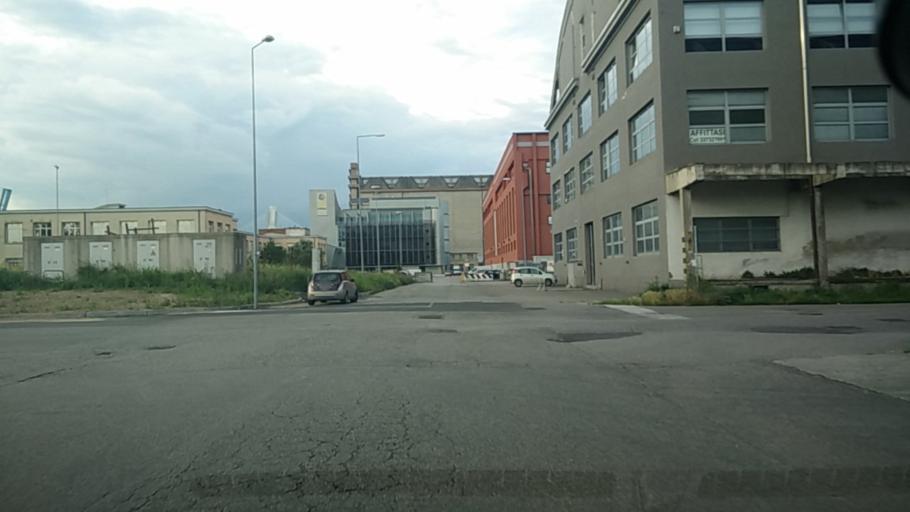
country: IT
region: Veneto
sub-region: Provincia di Venezia
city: Mestre
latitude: 45.4659
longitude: 12.2358
